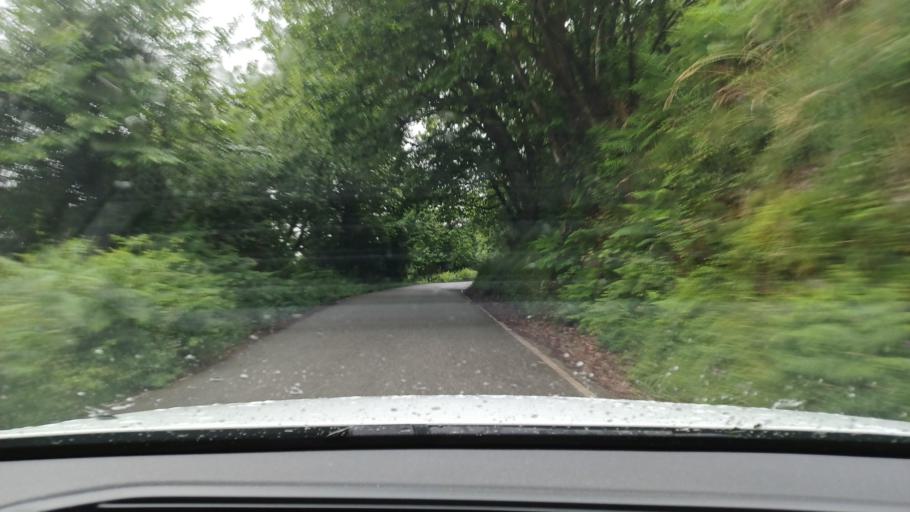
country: ES
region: Asturias
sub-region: Province of Asturias
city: Castandiello
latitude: 43.3091
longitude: -5.9258
